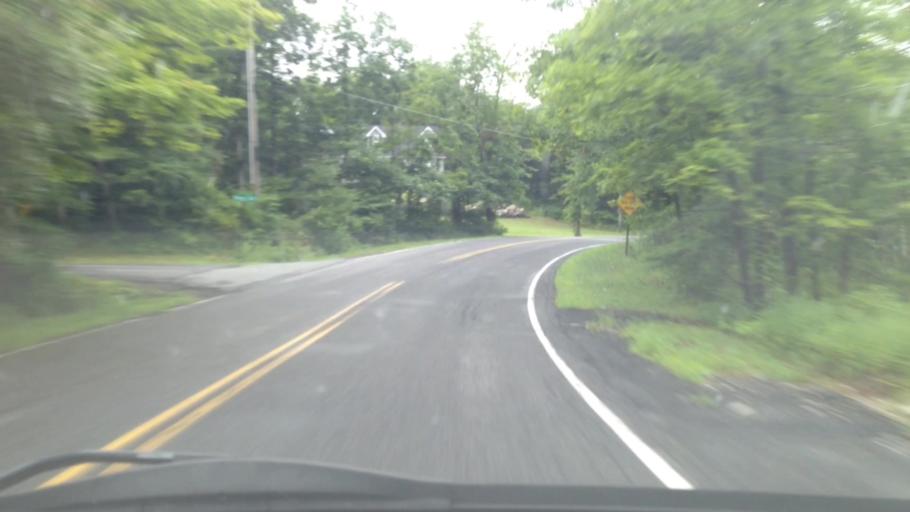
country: US
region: New York
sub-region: Ulster County
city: New Paltz
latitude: 41.7777
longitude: -74.0653
